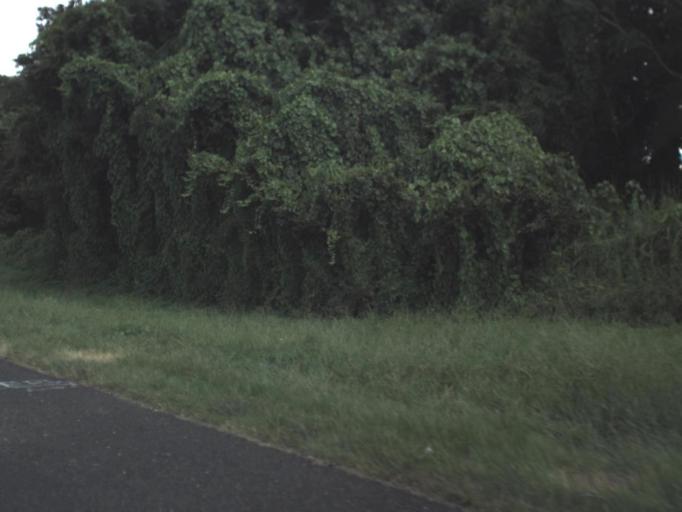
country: US
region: Florida
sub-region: Hillsborough County
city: Plant City
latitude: 27.9377
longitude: -82.1068
